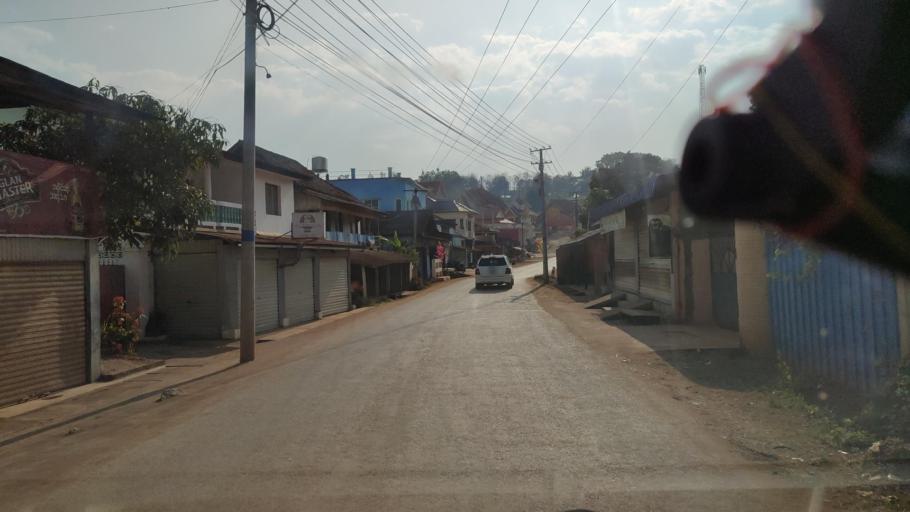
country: CN
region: Yunnan
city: Nayun
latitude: 21.8446
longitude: 99.6859
